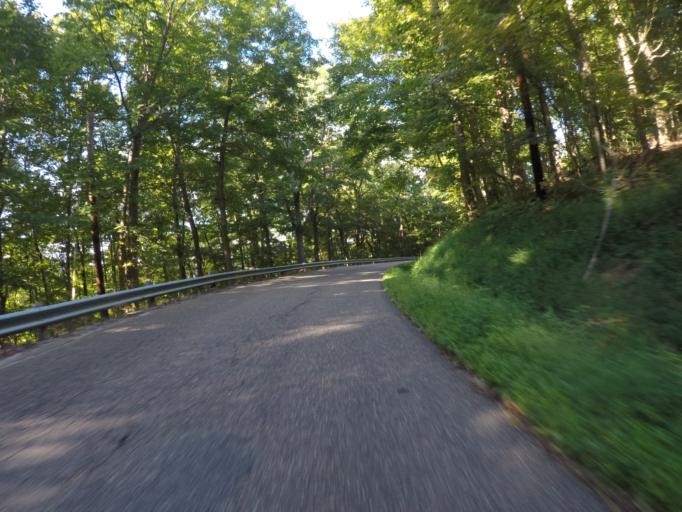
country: US
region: West Virginia
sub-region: Cabell County
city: Huntington
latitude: 38.4666
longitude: -82.4619
